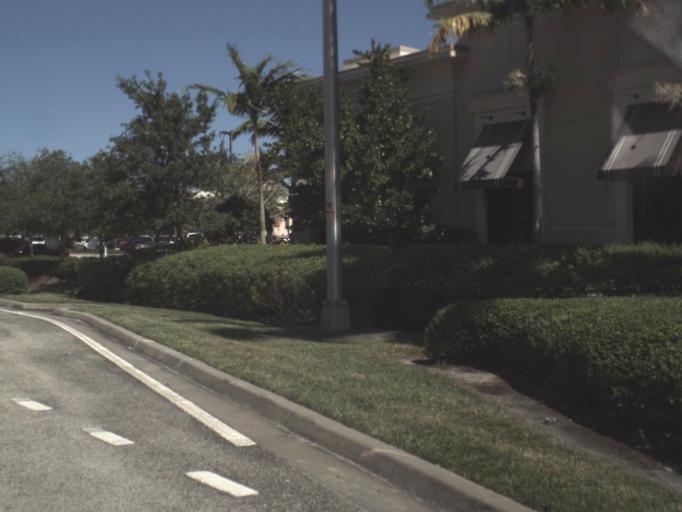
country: US
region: Florida
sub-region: Collier County
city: Naples Park
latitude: 26.2530
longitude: -81.8011
